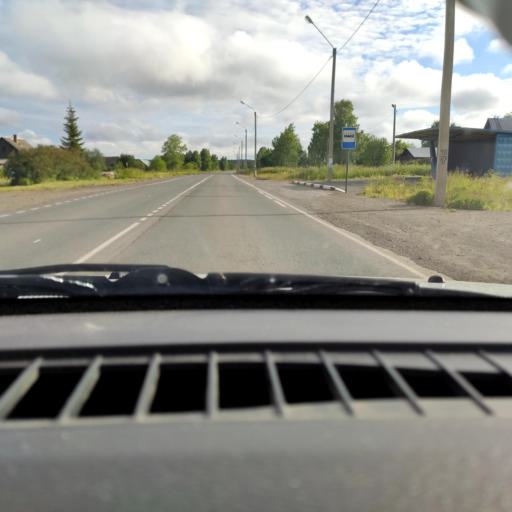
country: RU
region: Perm
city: Kungur
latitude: 57.3726
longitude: 56.9658
